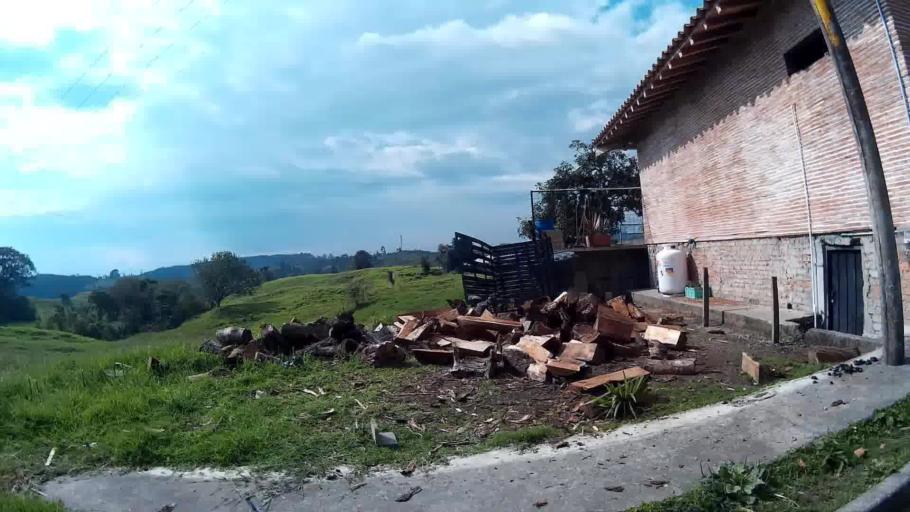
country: CO
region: Quindio
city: Filandia
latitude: 4.6887
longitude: -75.6074
